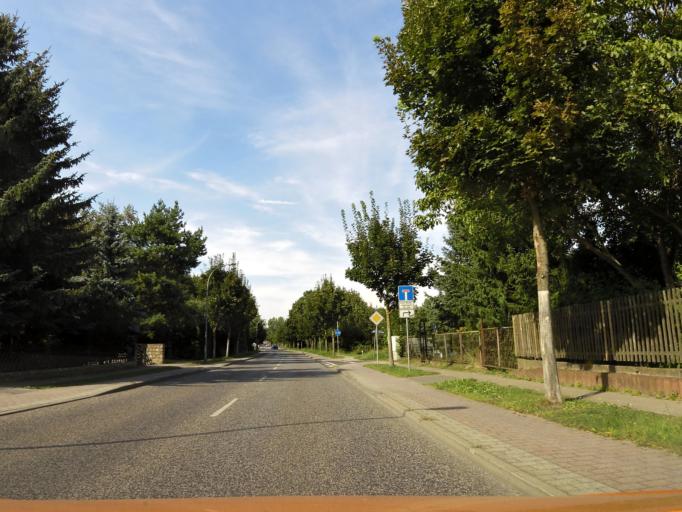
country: DE
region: Brandenburg
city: Teltow
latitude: 52.3907
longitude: 13.2460
